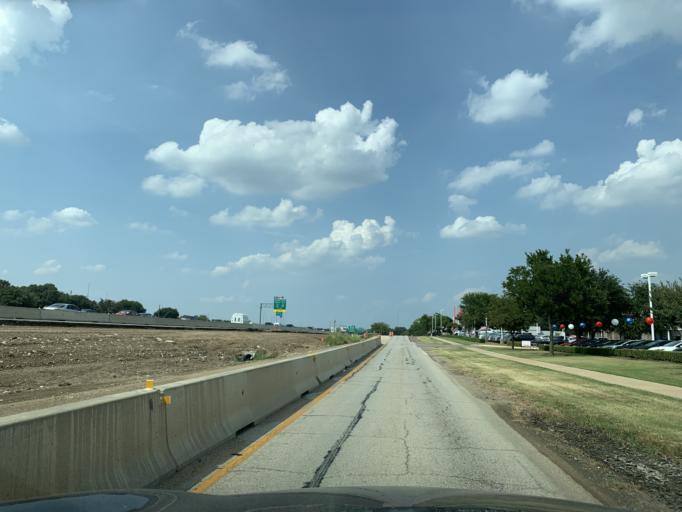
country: US
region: Texas
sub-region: Tarrant County
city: Richland Hills
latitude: 32.8123
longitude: -97.2078
